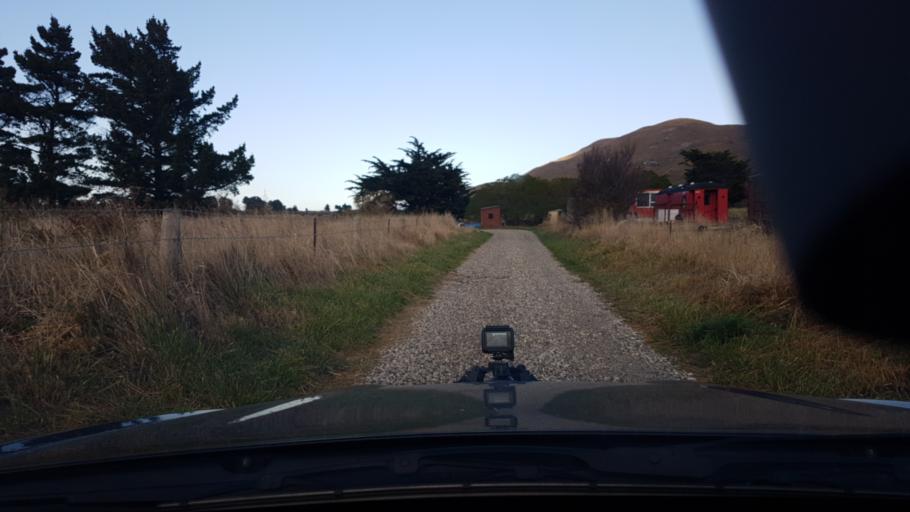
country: NZ
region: Marlborough
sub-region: Marlborough District
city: Blenheim
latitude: -41.9247
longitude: 174.0937
